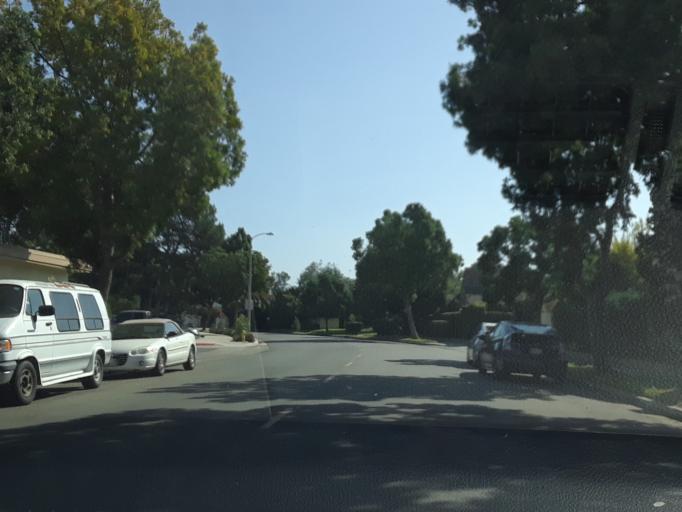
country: US
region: California
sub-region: Orange County
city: Irvine
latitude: 33.6604
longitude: -117.8259
